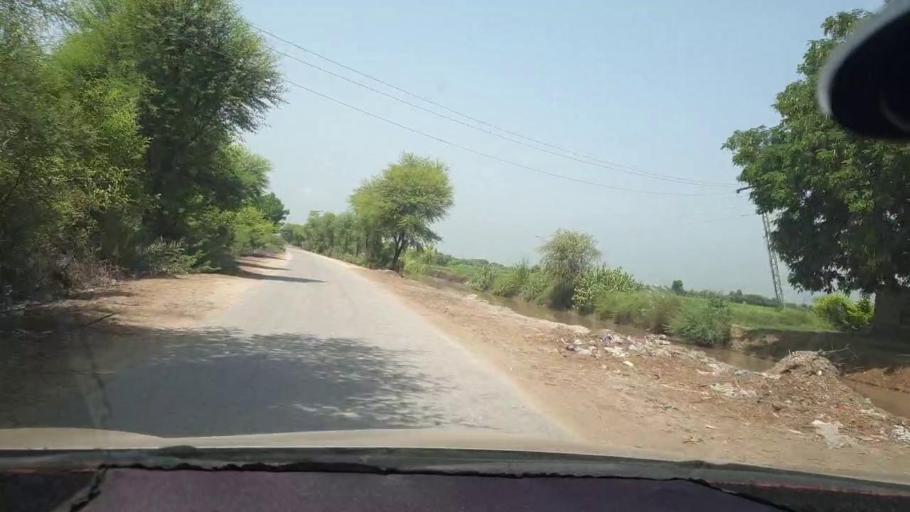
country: PK
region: Sindh
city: Kambar
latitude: 27.6354
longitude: 67.9817
